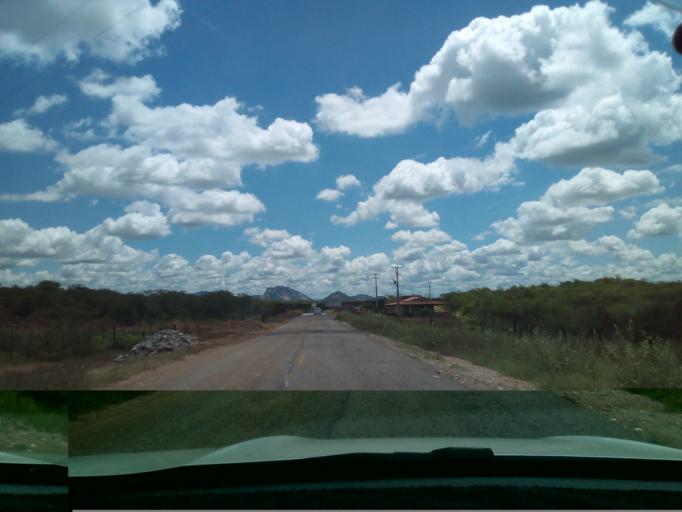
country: BR
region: Rio Grande do Norte
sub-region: Jardim De Piranhas
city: Jardim de Piranhas
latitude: -6.3733
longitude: -37.3805
